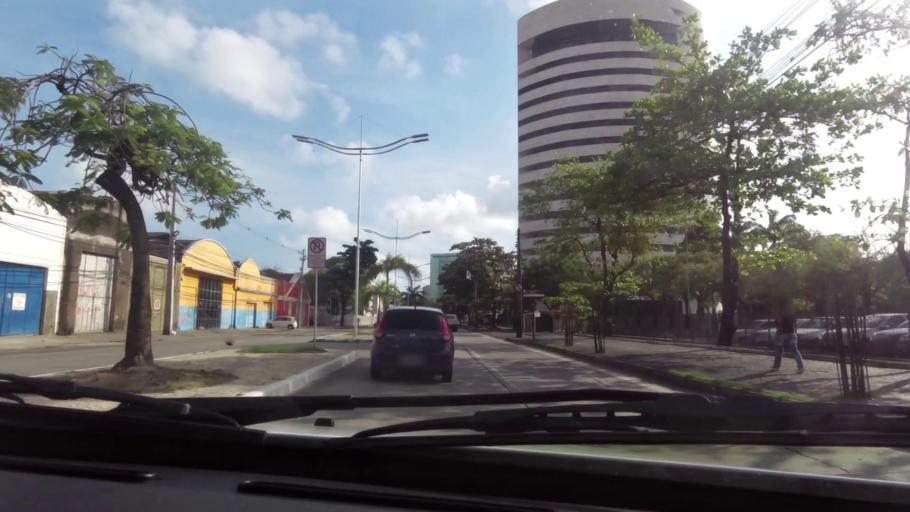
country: BR
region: Pernambuco
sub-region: Recife
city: Recife
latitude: -8.0596
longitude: -34.8728
